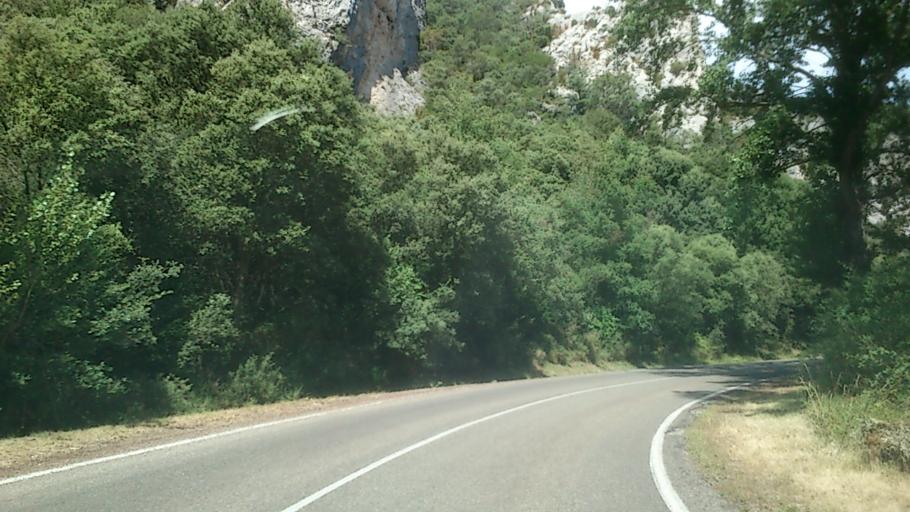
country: ES
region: Castille and Leon
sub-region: Provincia de Burgos
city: Frias
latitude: 42.7415
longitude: -3.3140
